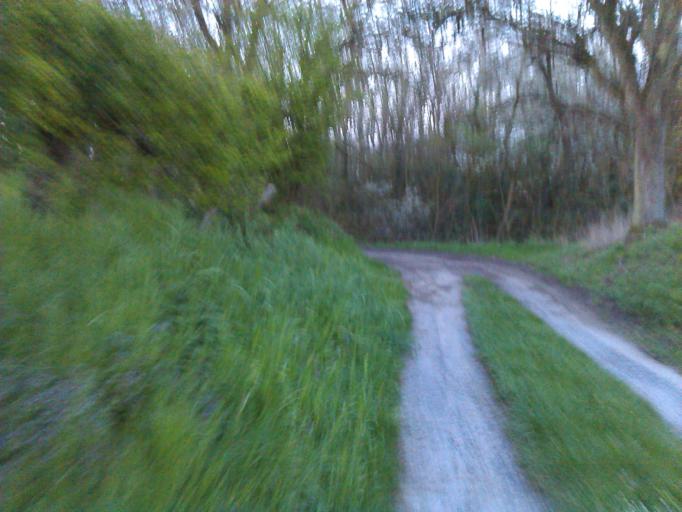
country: DE
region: Baden-Wuerttemberg
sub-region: Regierungsbezirk Stuttgart
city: Untereisesheim
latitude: 49.2152
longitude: 9.1817
